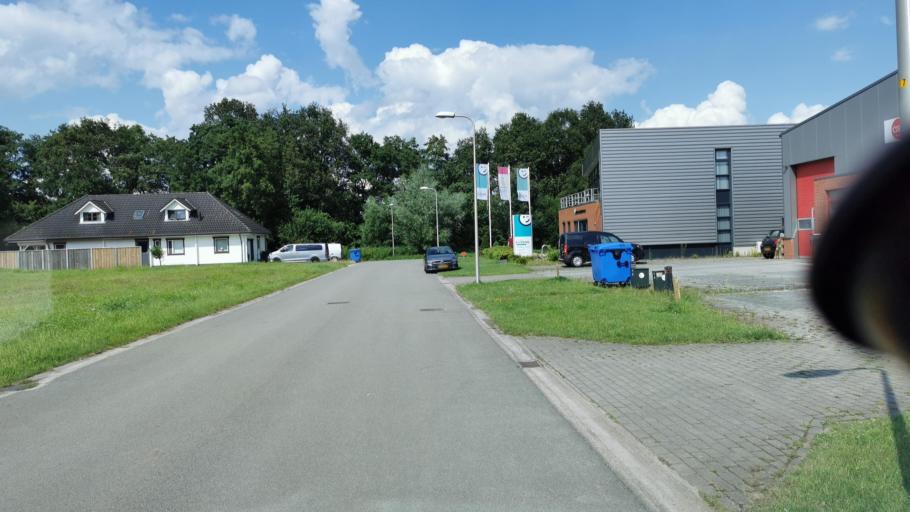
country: NL
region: Overijssel
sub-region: Gemeente Enschede
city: Enschede
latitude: 52.2267
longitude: 6.9496
